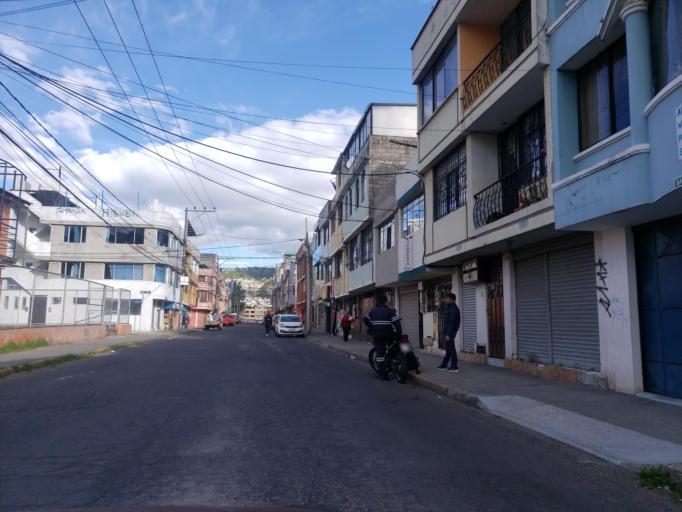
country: EC
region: Pichincha
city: Quito
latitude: -0.2655
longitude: -78.5392
